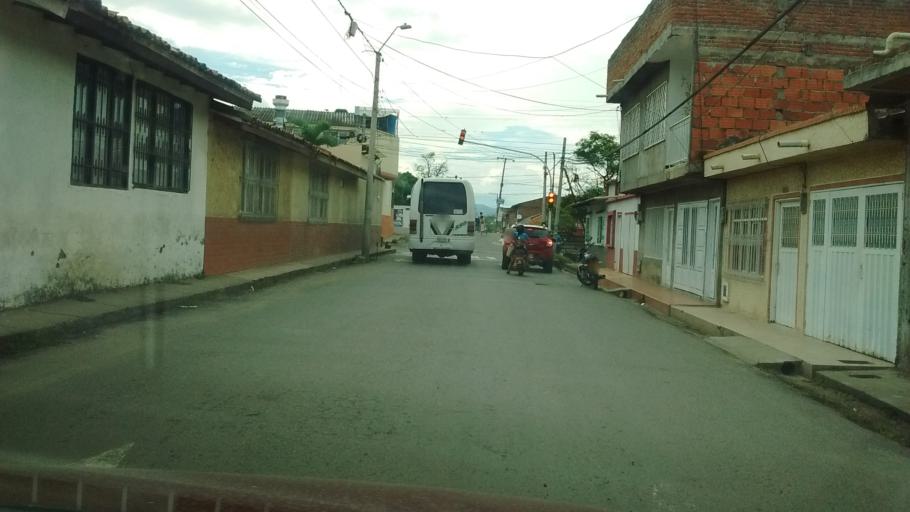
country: CO
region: Cauca
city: Santander de Quilichao
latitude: 3.0159
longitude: -76.4819
